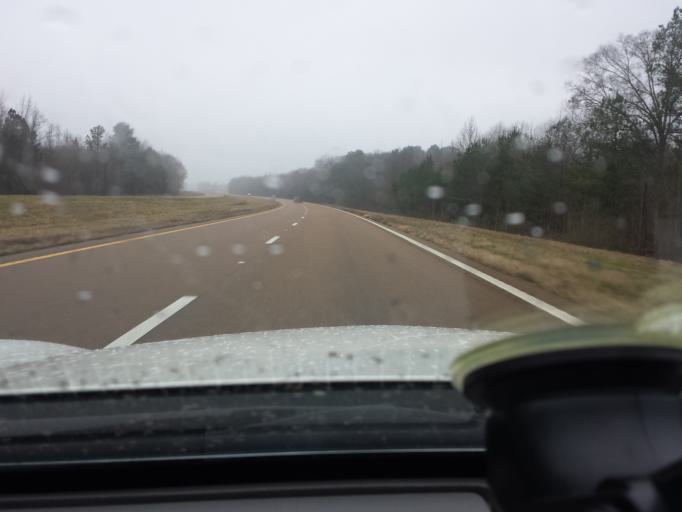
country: US
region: Mississippi
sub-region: Scott County
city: Morton
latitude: 32.5811
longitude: -89.7356
